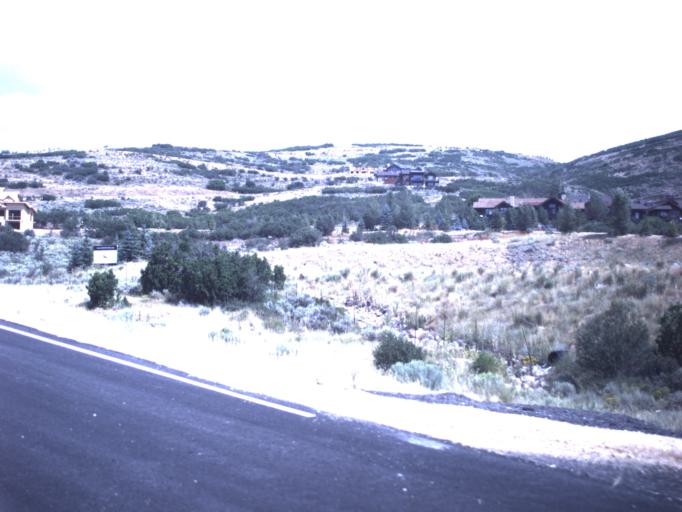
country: US
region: Utah
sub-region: Summit County
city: Park City
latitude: 40.6674
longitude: -111.4204
